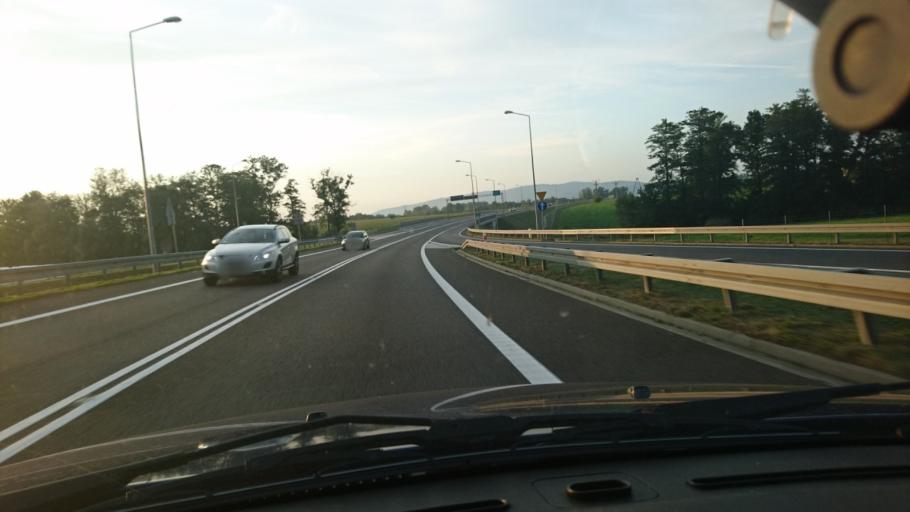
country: PL
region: Silesian Voivodeship
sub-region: Powiat zywiecki
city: Wieprz
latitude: 49.6584
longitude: 19.1671
